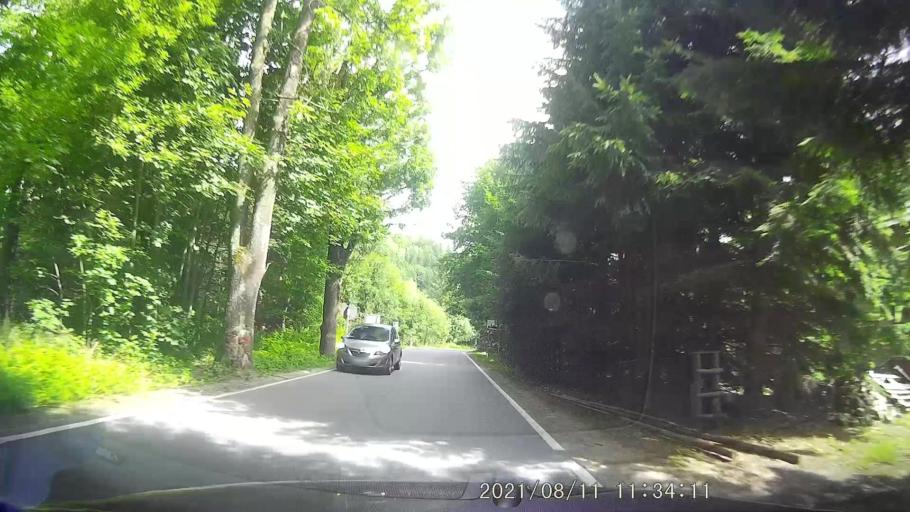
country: PL
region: Lower Silesian Voivodeship
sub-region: Powiat klodzki
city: Stronie Slaskie
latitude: 50.2624
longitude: 16.8243
